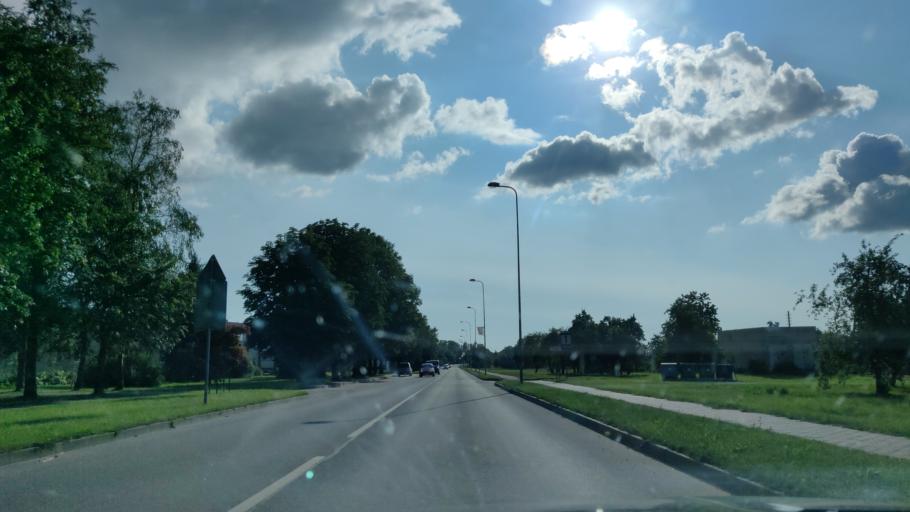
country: LT
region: Klaipedos apskritis
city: Gargzdai
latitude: 55.7178
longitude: 21.4722
